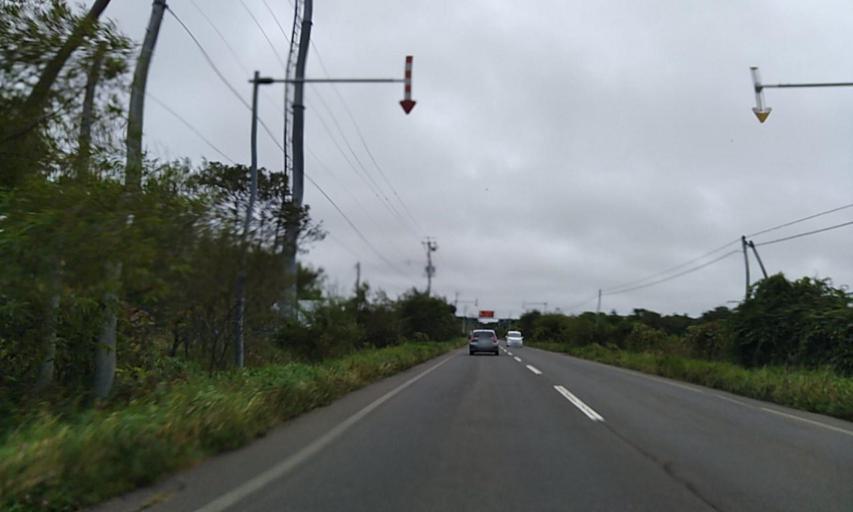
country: JP
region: Hokkaido
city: Nemuro
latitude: 43.2615
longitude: 145.4185
